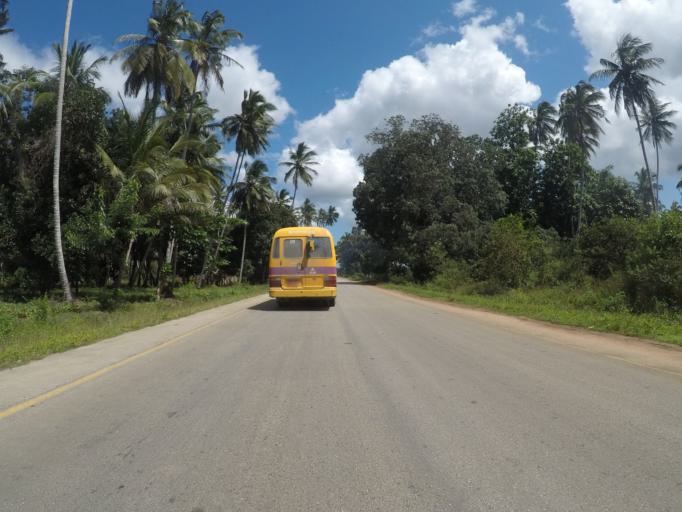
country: TZ
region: Zanzibar Central/South
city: Koani
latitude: -6.1516
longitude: 39.3296
